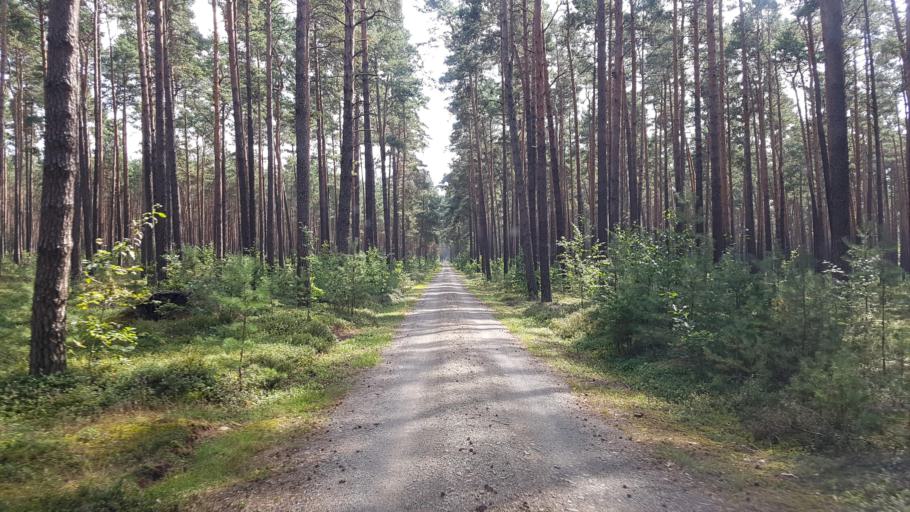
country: DE
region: Brandenburg
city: Hohenbucko
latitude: 51.7876
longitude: 13.5206
